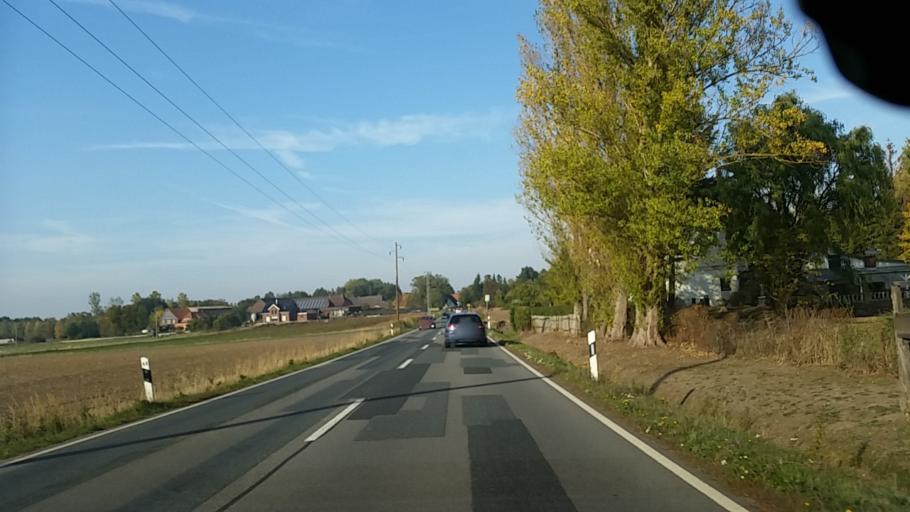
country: DE
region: Lower Saxony
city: Konigslutter am Elm
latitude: 52.3170
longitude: 10.8176
